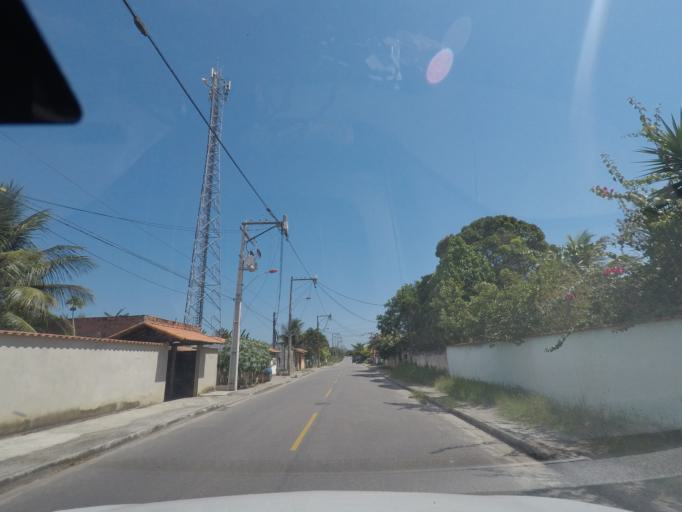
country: BR
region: Rio de Janeiro
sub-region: Marica
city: Marica
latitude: -22.9605
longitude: -42.9631
